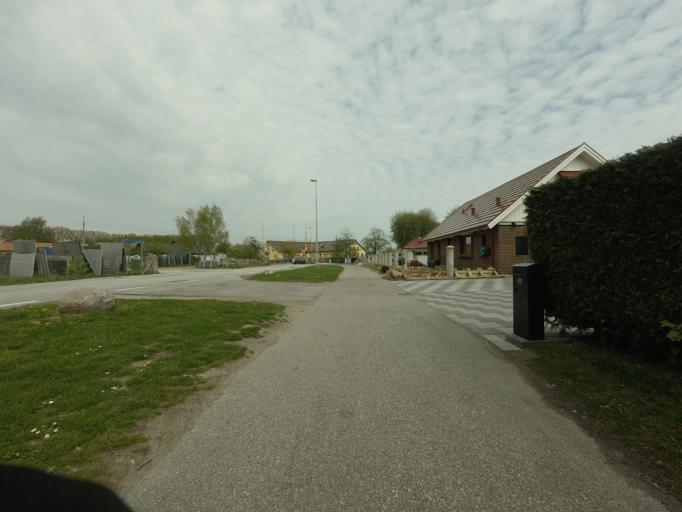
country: SE
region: Skane
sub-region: Malmo
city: Oxie
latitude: 55.5444
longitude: 13.0822
